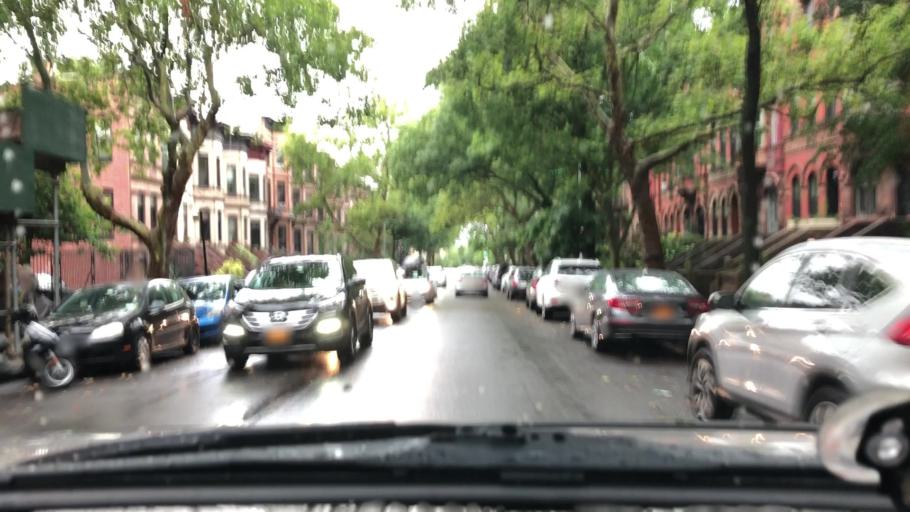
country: US
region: New York
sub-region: Kings County
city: Brooklyn
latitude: 40.6737
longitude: -73.9735
